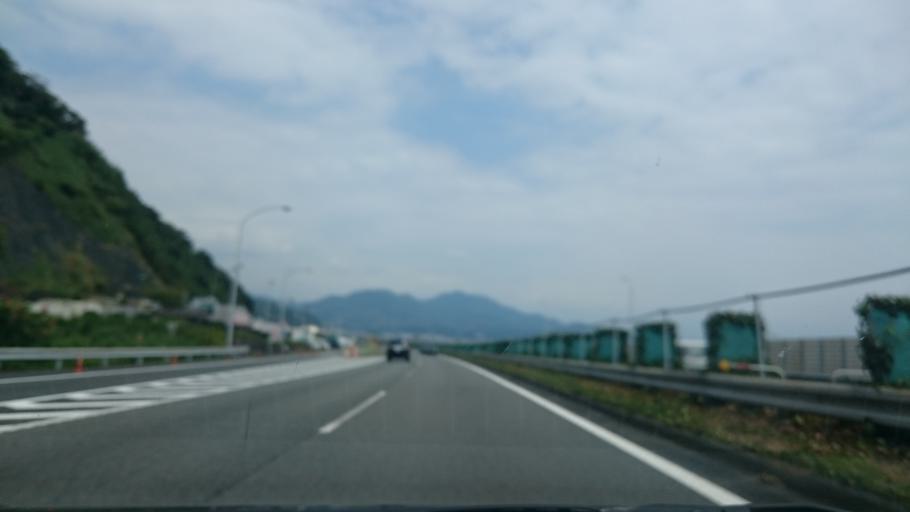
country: JP
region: Shizuoka
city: Fujinomiya
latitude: 35.0759
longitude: 138.5457
